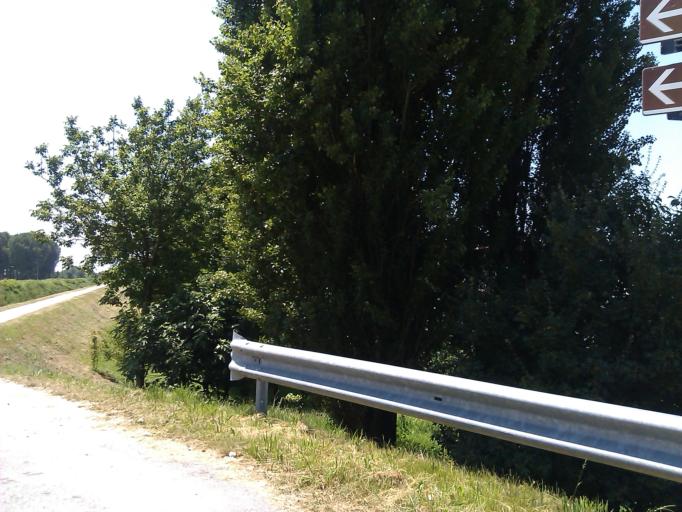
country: IT
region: Veneto
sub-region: Provincia di Padova
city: Camposampiero
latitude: 45.5752
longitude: 11.9399
